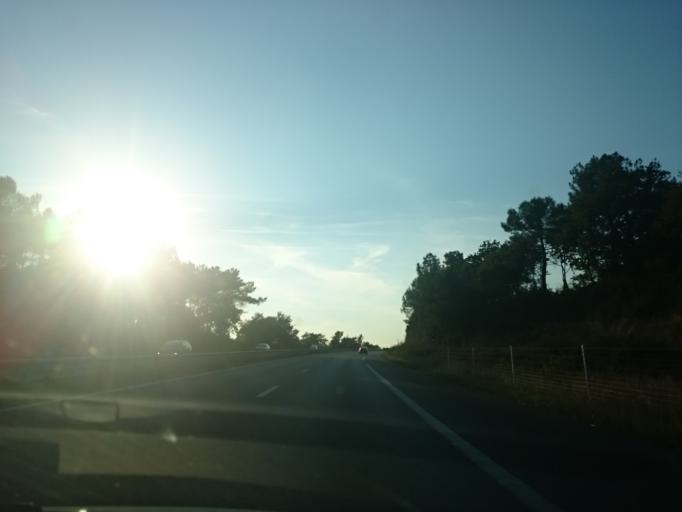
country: FR
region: Brittany
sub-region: Departement du Morbihan
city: Ambon
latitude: 47.5964
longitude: -2.5737
